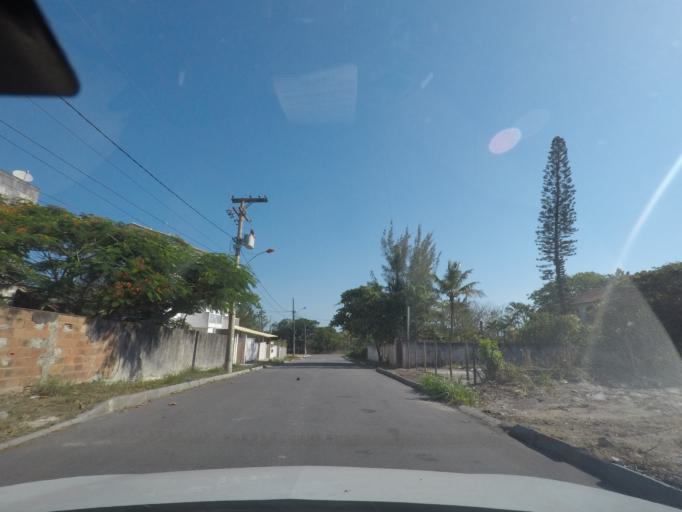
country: BR
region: Rio de Janeiro
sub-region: Marica
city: Marica
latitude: -22.9705
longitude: -42.9190
